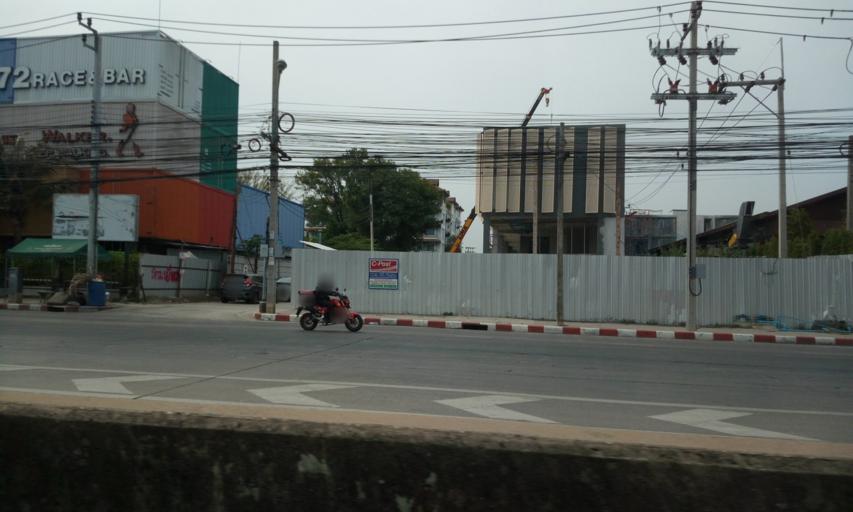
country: TH
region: Bangkok
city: Lat Krabang
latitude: 13.7218
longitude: 100.7750
